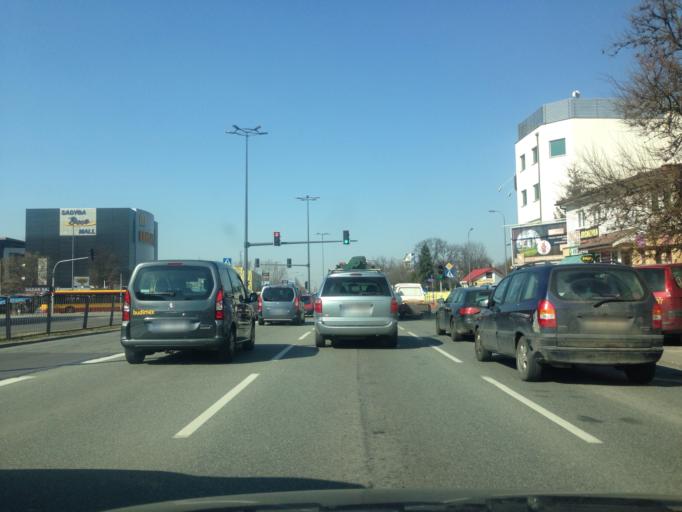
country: PL
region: Masovian Voivodeship
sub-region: Warszawa
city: Mokotow
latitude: 52.1862
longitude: 21.0645
